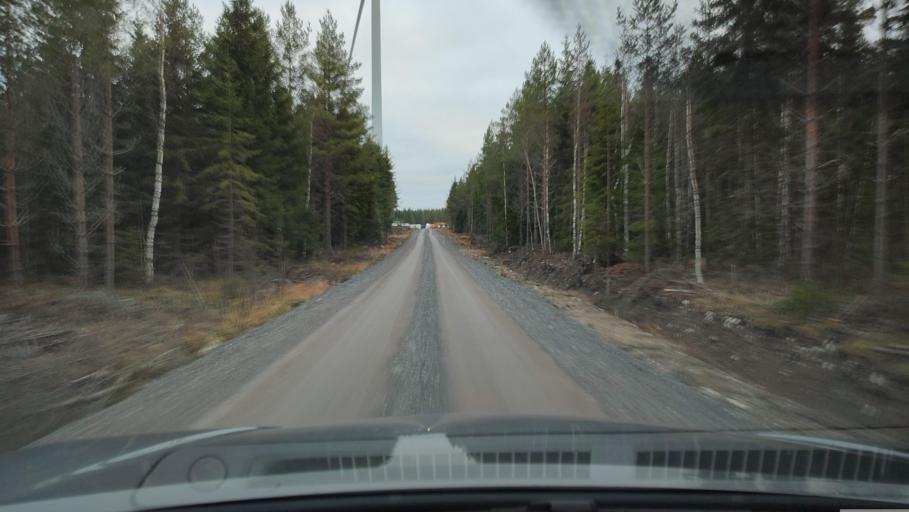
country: FI
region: Southern Ostrobothnia
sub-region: Suupohja
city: Karijoki
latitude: 62.1852
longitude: 21.5625
